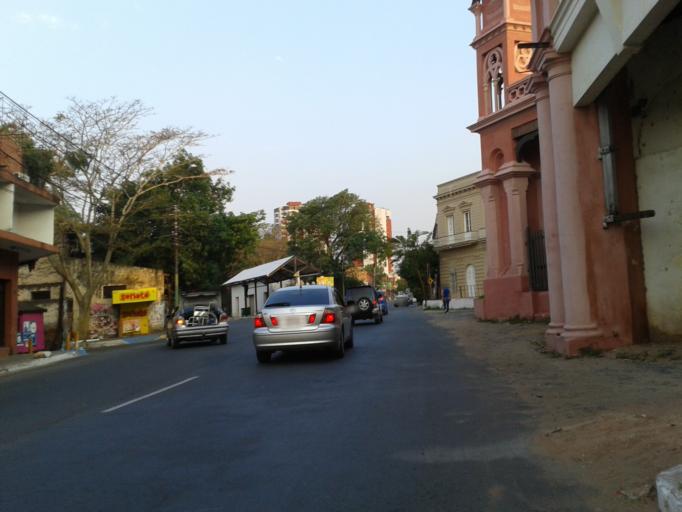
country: PY
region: Asuncion
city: Asuncion
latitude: -25.2837
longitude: -57.6295
